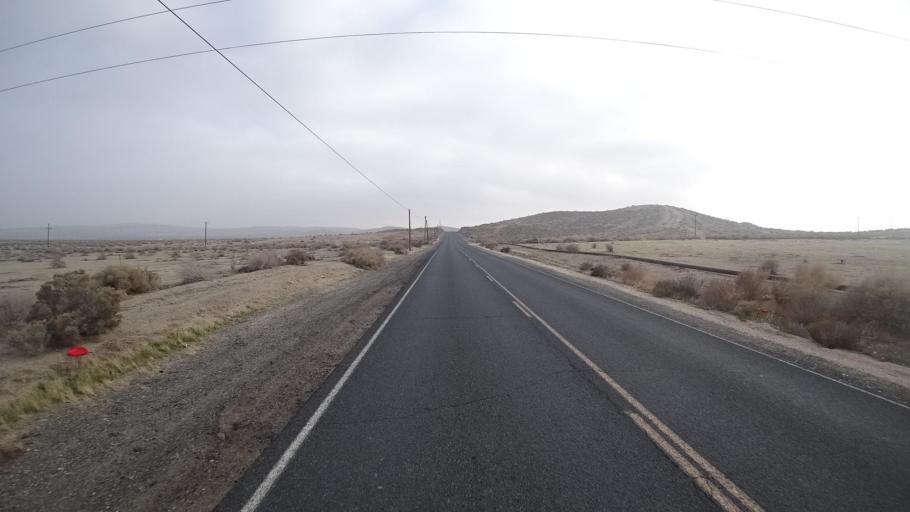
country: US
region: California
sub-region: Kern County
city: Ford City
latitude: 35.1946
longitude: -119.4457
